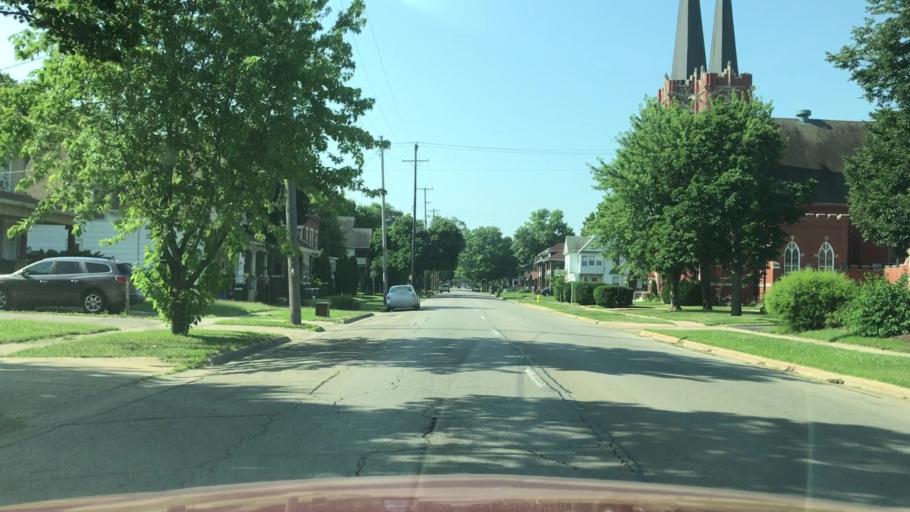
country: US
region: Illinois
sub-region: Winnebago County
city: Rockford
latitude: 42.2512
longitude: -89.0824
